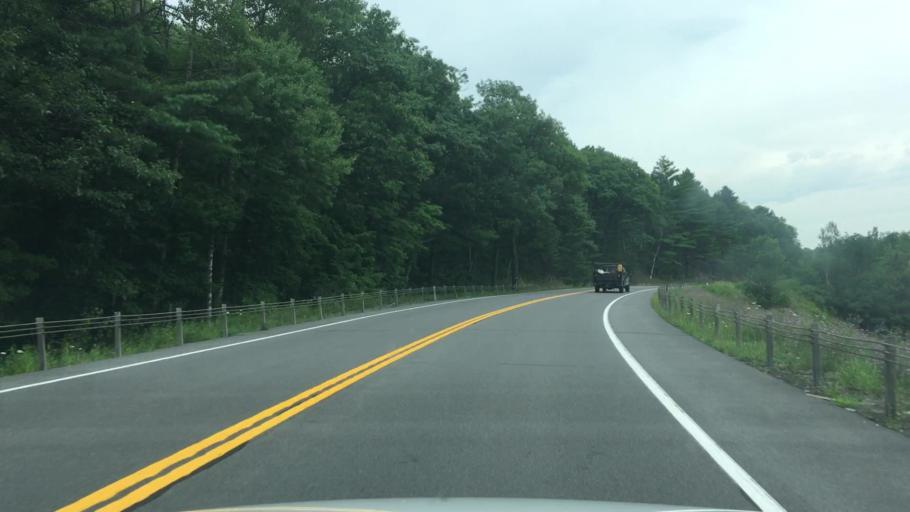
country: US
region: New York
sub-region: Essex County
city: Keeseville
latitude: 44.4590
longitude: -73.6290
